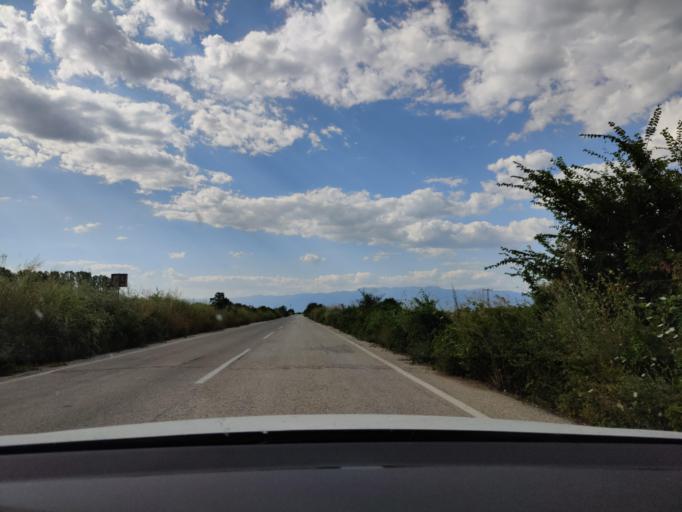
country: GR
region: Central Macedonia
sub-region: Nomos Serron
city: Strymoniko
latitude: 41.0718
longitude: 23.3002
